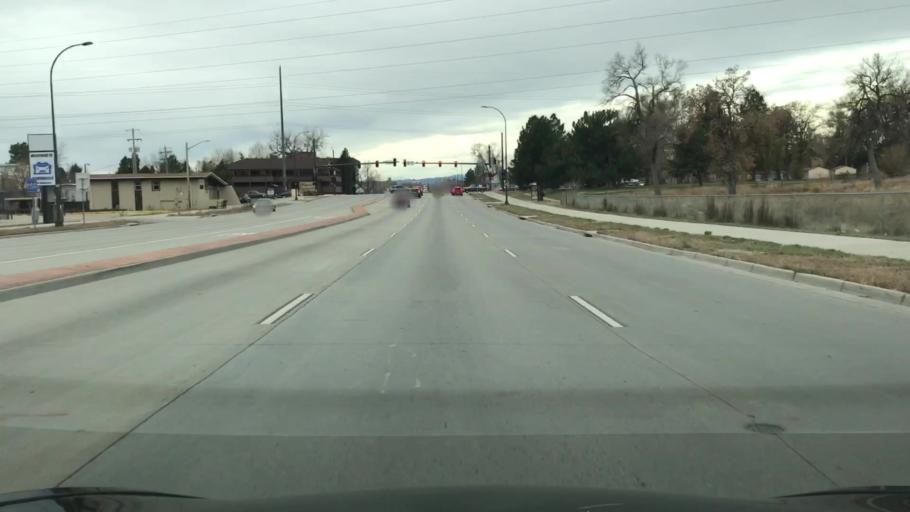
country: US
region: Colorado
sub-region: Jefferson County
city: Edgewater
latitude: 39.7346
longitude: -105.0816
